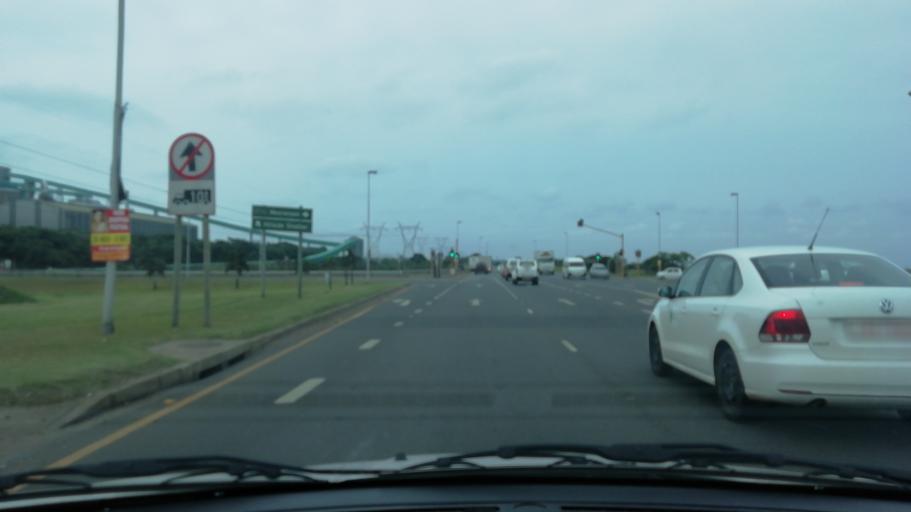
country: ZA
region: KwaZulu-Natal
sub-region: uThungulu District Municipality
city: Richards Bay
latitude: -28.7692
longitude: 32.0350
